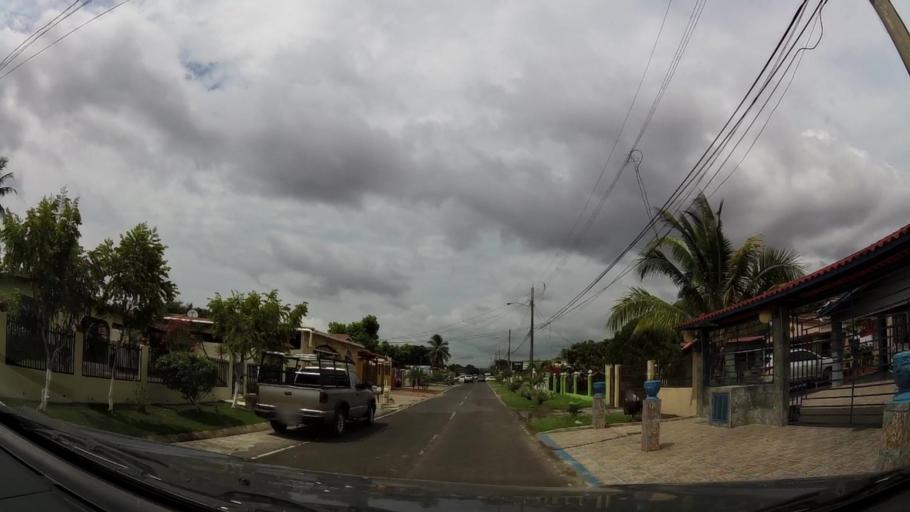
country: PA
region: Panama
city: San Miguelito
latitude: 9.0446
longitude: -79.4218
